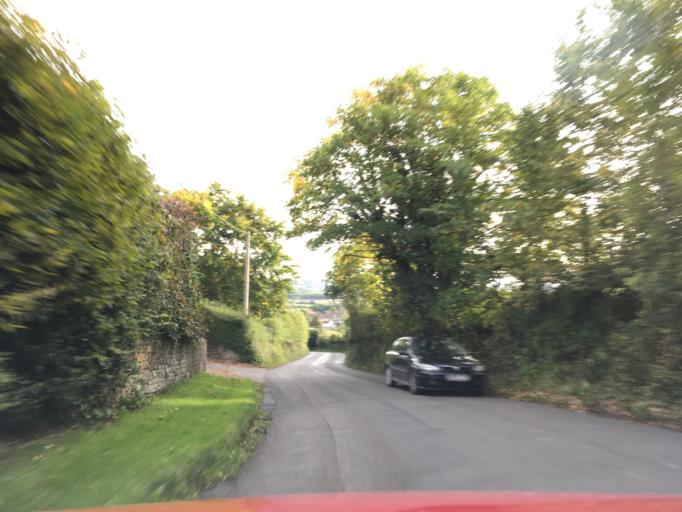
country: GB
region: England
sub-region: South Gloucestershire
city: Almondsbury
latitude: 51.5807
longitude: -2.5643
